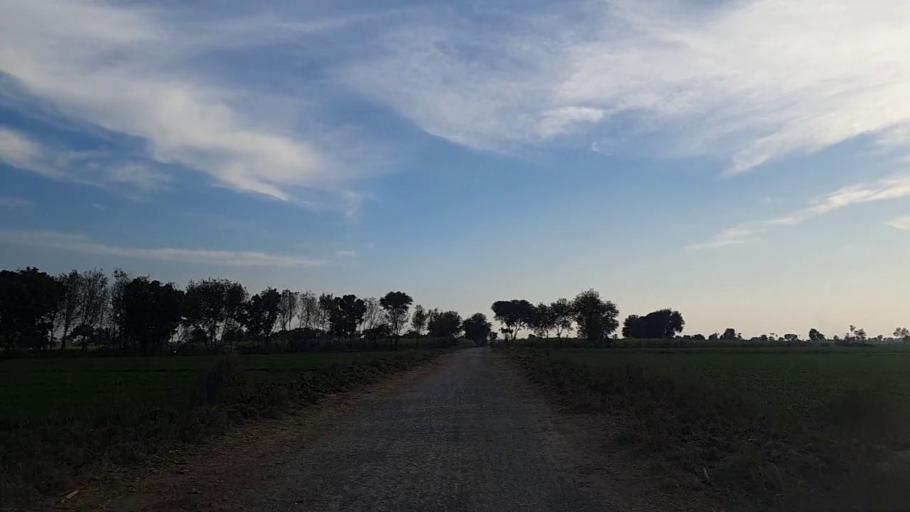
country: PK
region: Sindh
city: Bandhi
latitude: 26.5563
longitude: 68.2809
